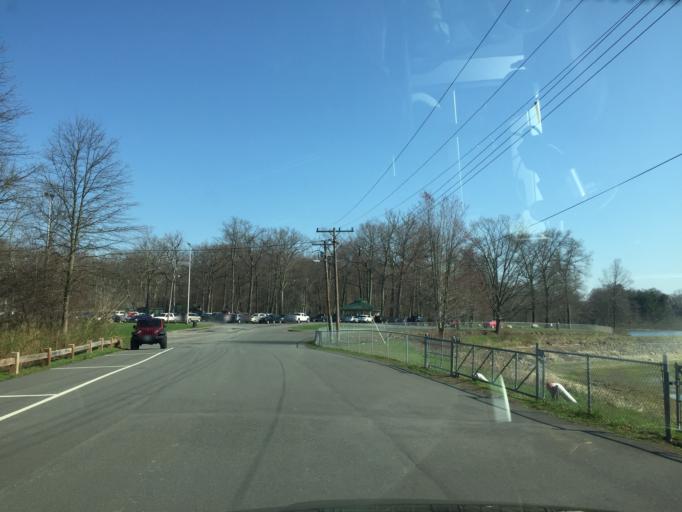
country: US
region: Connecticut
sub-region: Hartford County
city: Wethersfield
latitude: 41.6915
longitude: -72.6663
